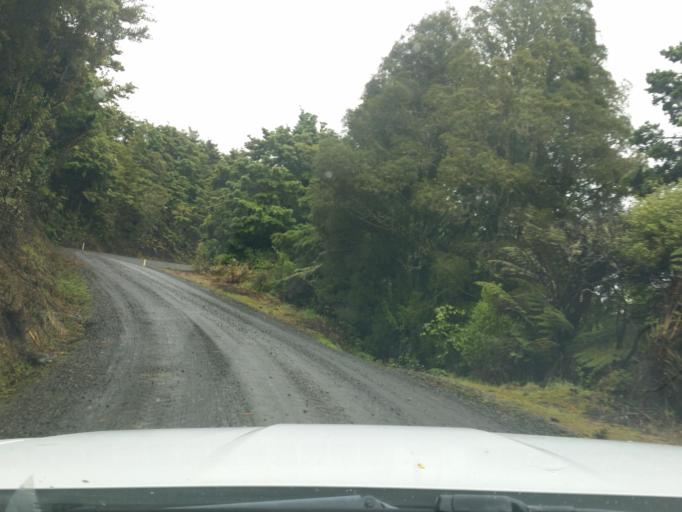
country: NZ
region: Northland
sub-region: Kaipara District
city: Dargaville
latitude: -35.7617
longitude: 173.9302
